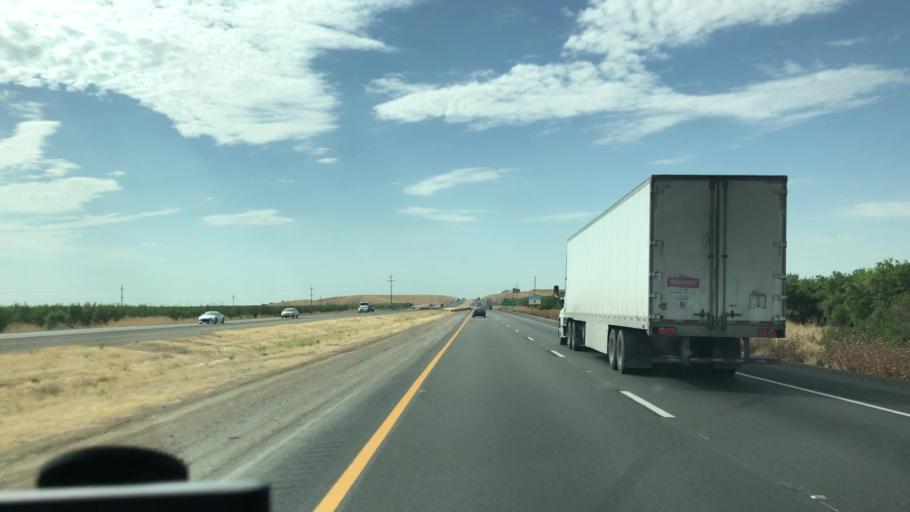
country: US
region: California
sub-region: Stanislaus County
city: Patterson
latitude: 37.4068
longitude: -121.1449
